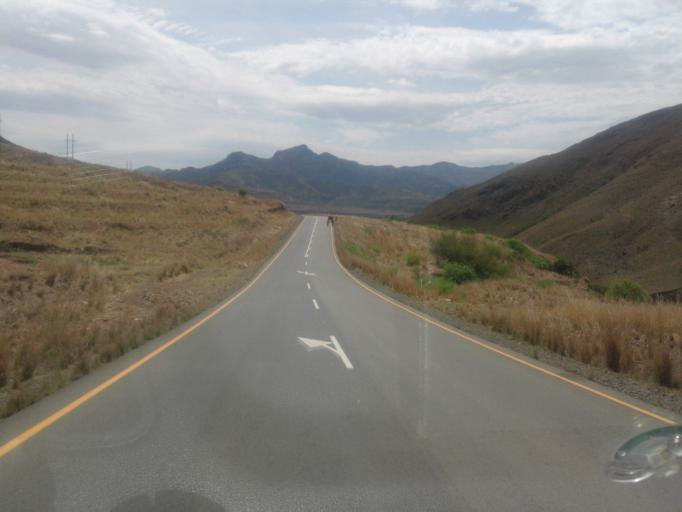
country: LS
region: Qacha's Nek
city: Qacha's Nek
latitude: -30.0851
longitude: 28.6335
